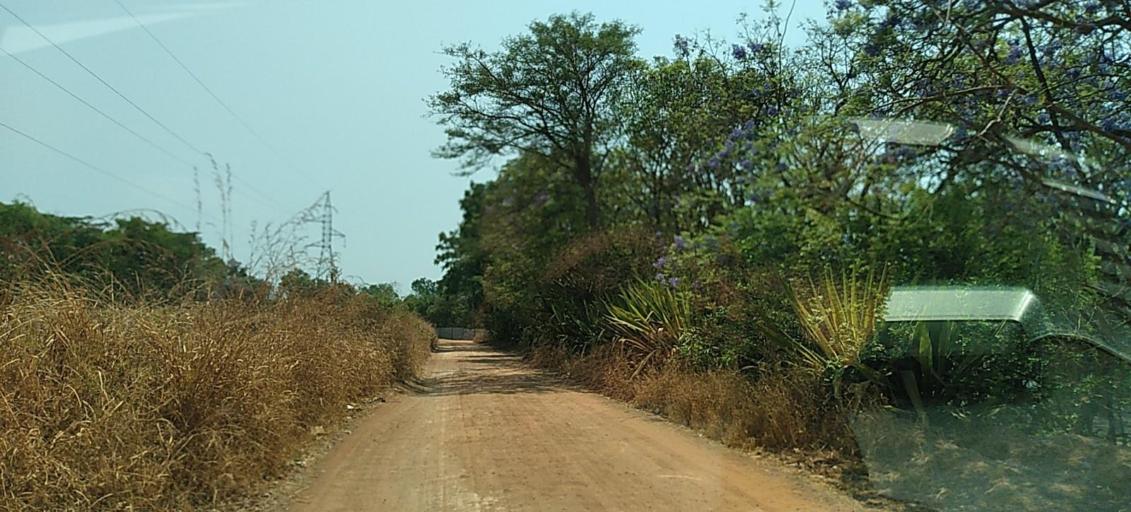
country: ZM
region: Copperbelt
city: Chambishi
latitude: -12.6185
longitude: 27.9487
